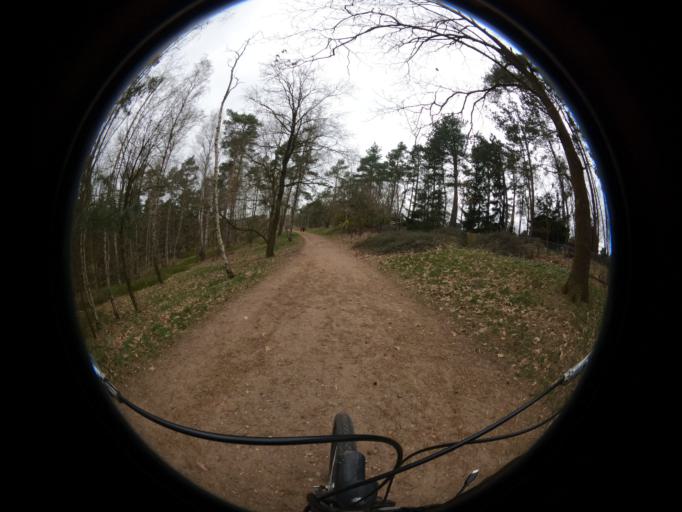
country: DE
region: Lower Saxony
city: Neu Wulmstorf
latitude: 53.4629
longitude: 9.8471
